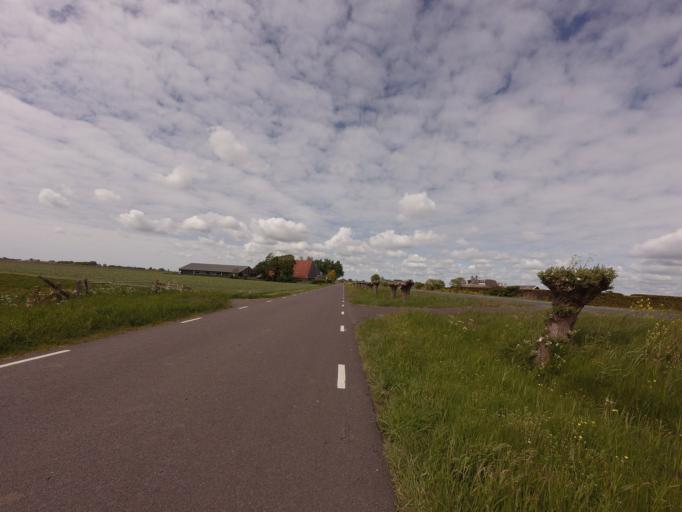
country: NL
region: Friesland
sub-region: Sudwest Fryslan
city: Woudsend
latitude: 52.9600
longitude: 5.6518
